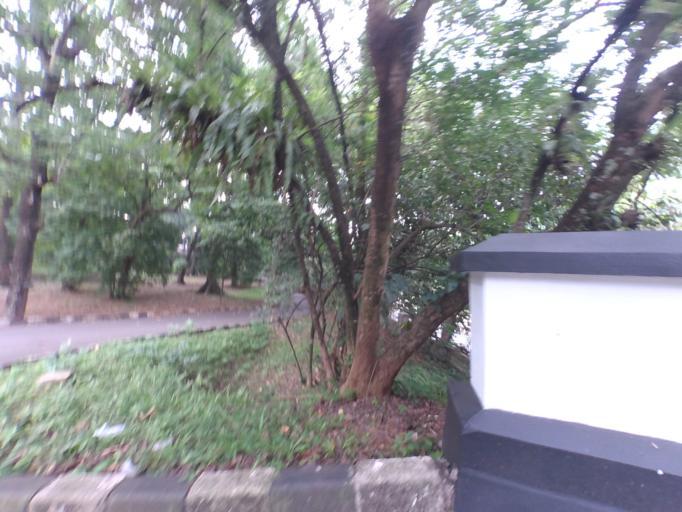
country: ID
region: West Java
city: Bogor
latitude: -6.5937
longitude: 106.8002
